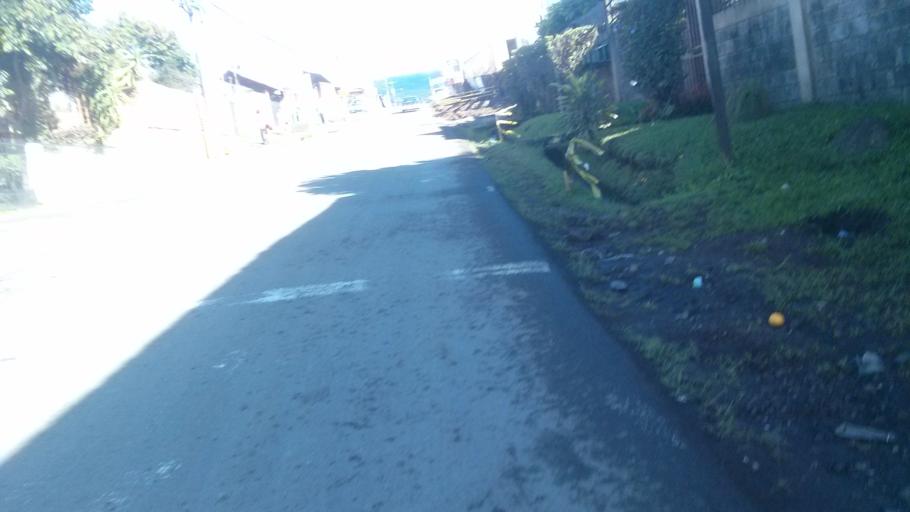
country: CR
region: Heredia
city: Angeles
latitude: 10.0133
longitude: -84.0543
